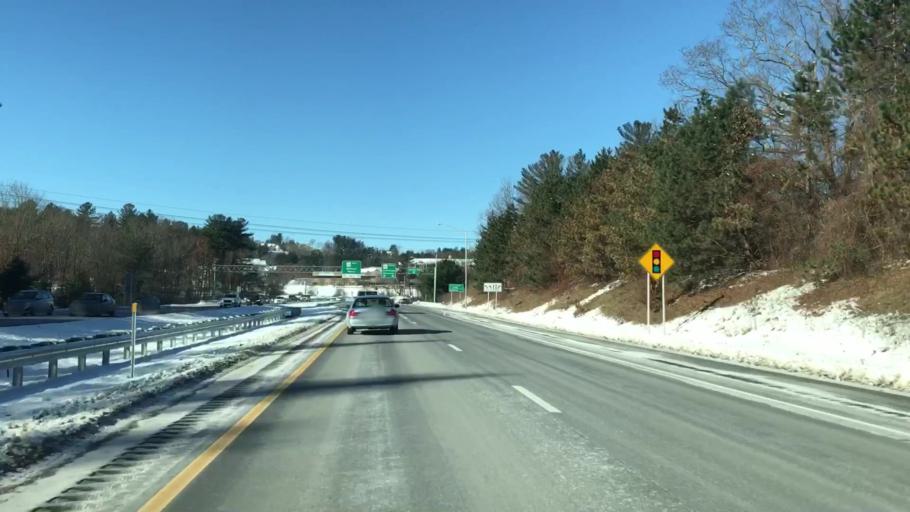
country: US
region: New Hampshire
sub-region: Hillsborough County
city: Bedford
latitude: 42.9590
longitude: -71.4979
